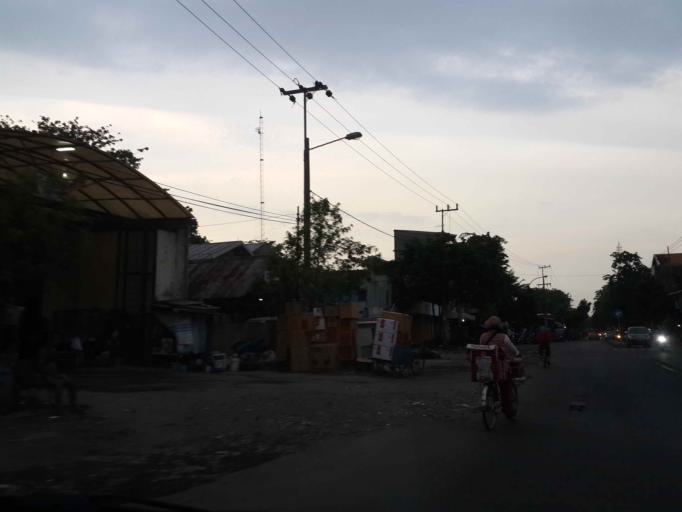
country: ID
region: East Java
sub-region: Kota Surabaya
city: Surabaya
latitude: -7.2542
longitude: 112.7282
